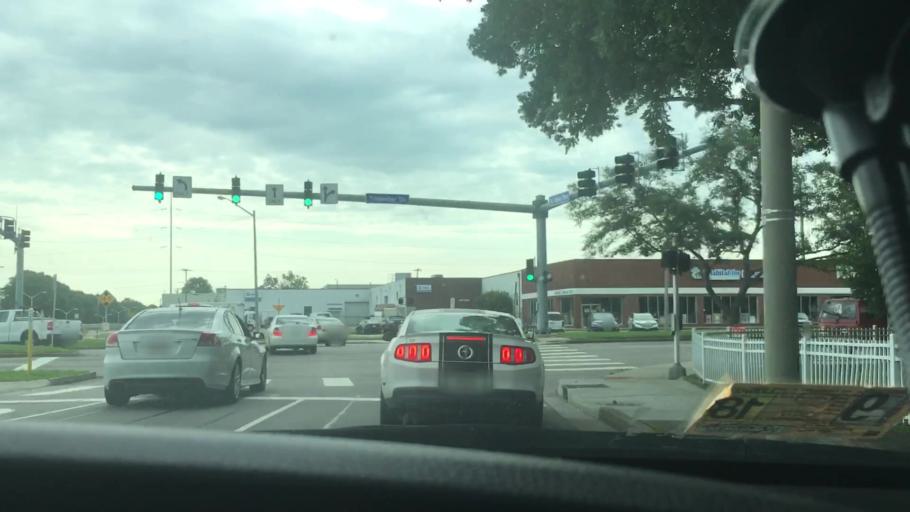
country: US
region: Virginia
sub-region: City of Norfolk
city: Norfolk
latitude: 36.8544
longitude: -76.2750
